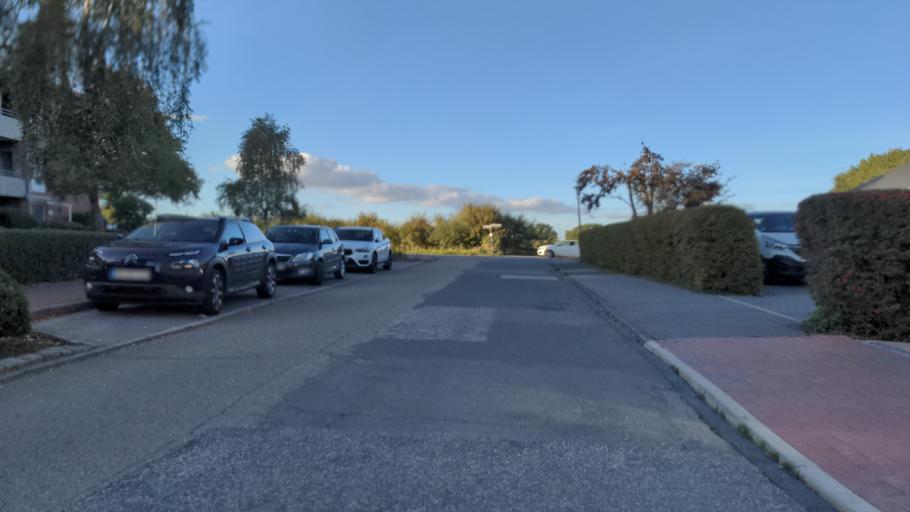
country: DE
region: Schleswig-Holstein
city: Neustadt in Holstein
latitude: 54.0929
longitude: 10.8492
